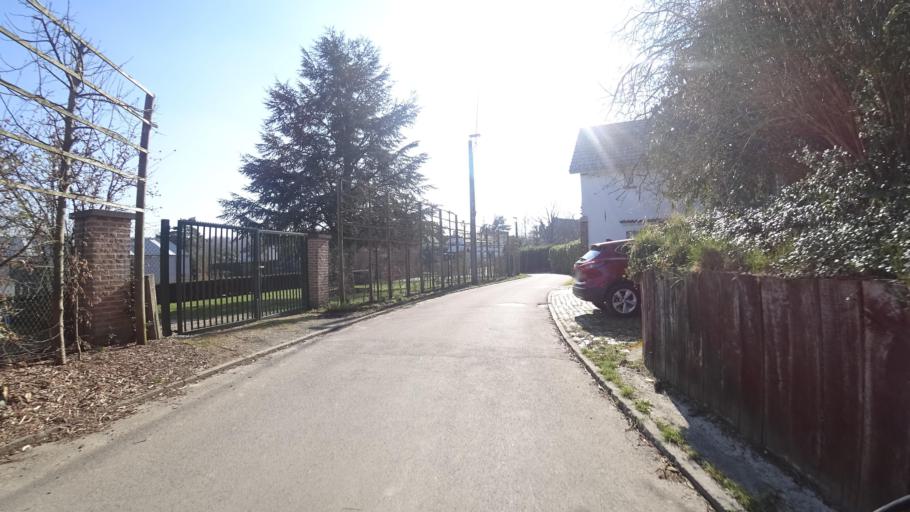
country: BE
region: Wallonia
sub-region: Province du Brabant Wallon
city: Court-Saint-Etienne
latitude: 50.6216
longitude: 4.5474
